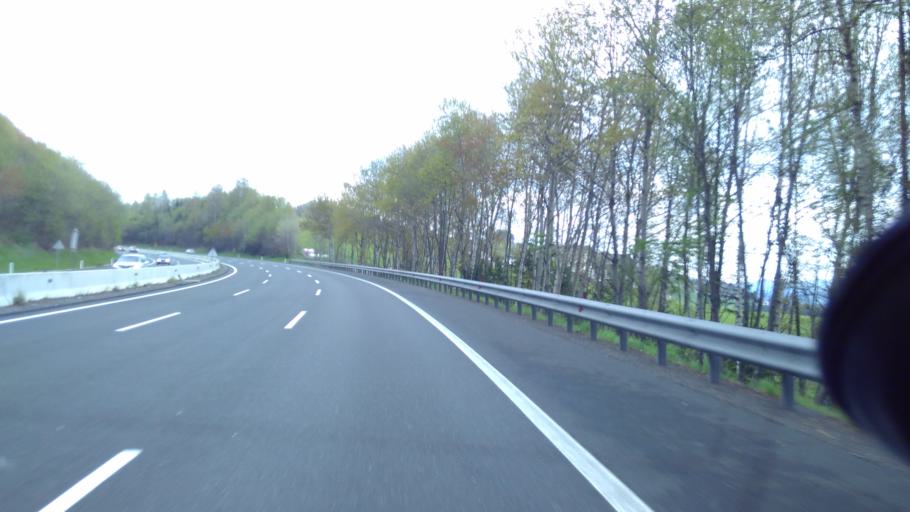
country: AT
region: Carinthia
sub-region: Politischer Bezirk Wolfsberg
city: Preitenegg
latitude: 46.9339
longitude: 14.8670
